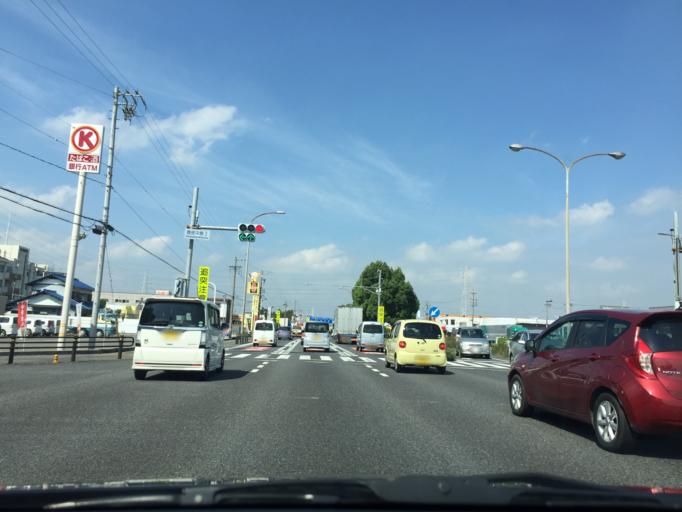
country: JP
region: Gifu
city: Kasamatsucho
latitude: 35.3884
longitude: 136.7513
